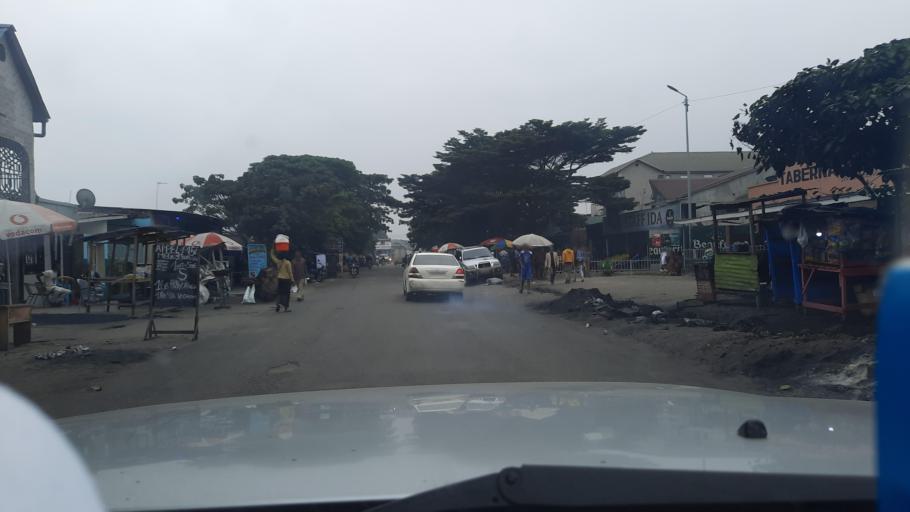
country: CD
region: Kinshasa
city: Masina
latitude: -4.3881
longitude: 15.3466
